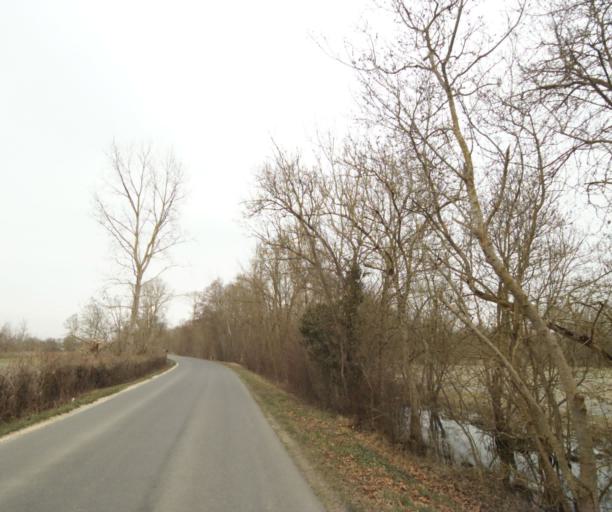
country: FR
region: Poitou-Charentes
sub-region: Departement des Deux-Sevres
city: Bessines
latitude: 46.3051
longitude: -0.5165
